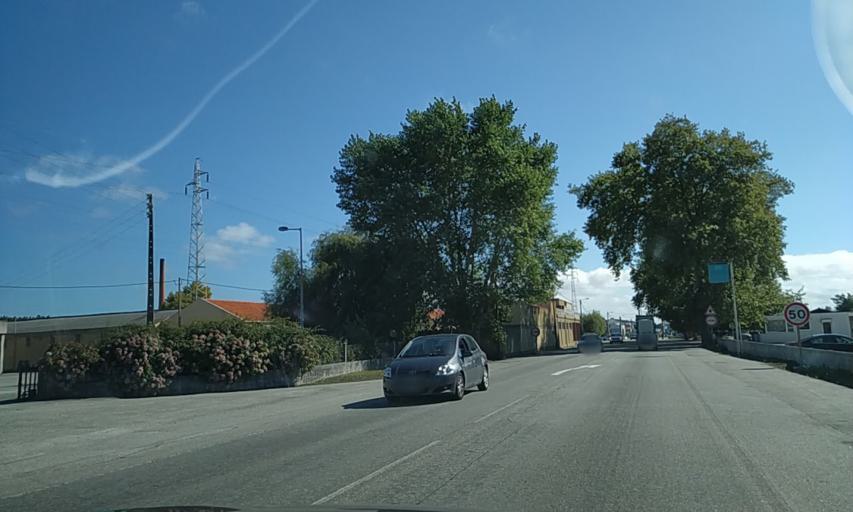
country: PT
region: Aveiro
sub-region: Aveiro
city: Aveiro
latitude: 40.6611
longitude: -8.6134
